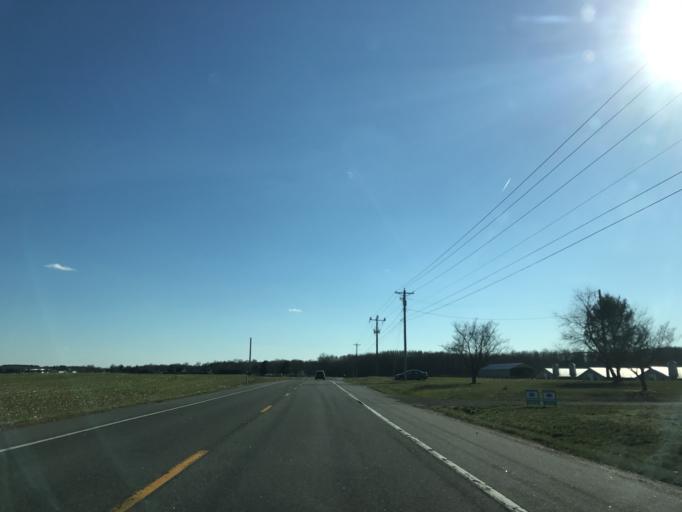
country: US
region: Maryland
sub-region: Queen Anne's County
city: Kingstown
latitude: 39.1590
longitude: -75.8640
